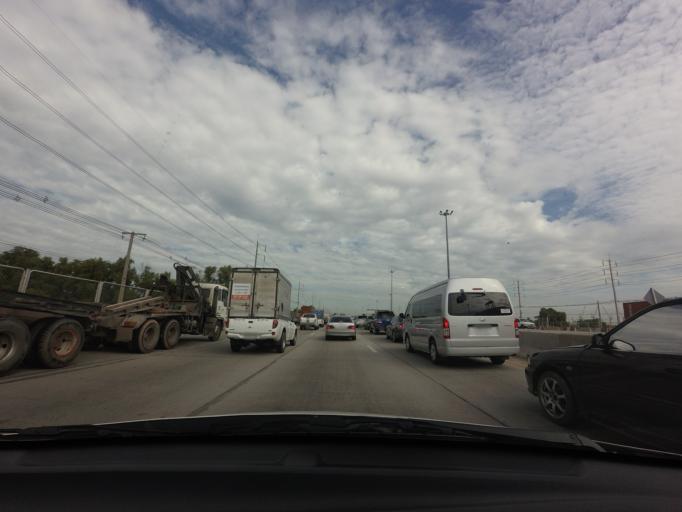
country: TH
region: Pathum Thani
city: Thanyaburi
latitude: 13.9761
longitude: 100.7128
